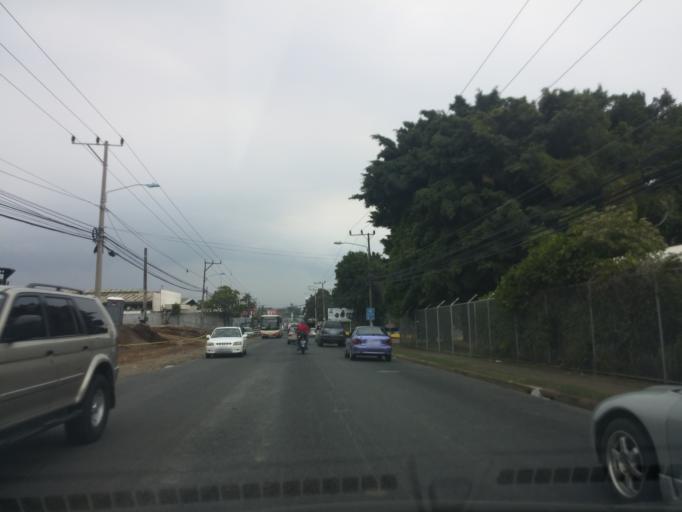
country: CR
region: Heredia
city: Llorente
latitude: 9.9821
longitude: -84.1535
